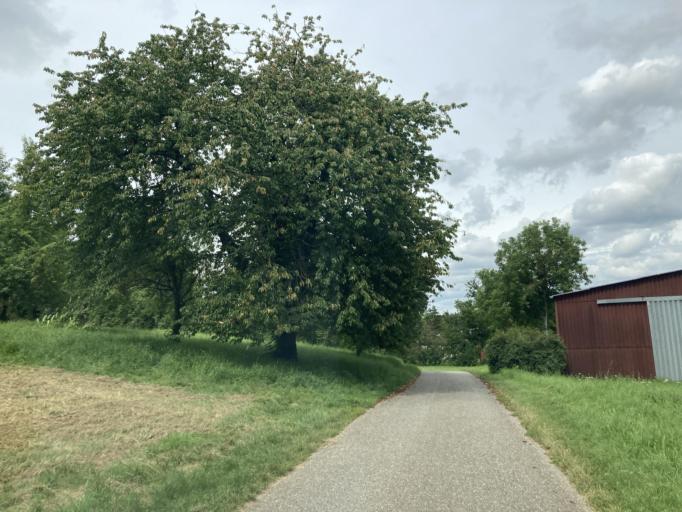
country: DE
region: Baden-Wuerttemberg
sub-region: Regierungsbezirk Stuttgart
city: Ittlingen
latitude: 49.2128
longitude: 8.9197
